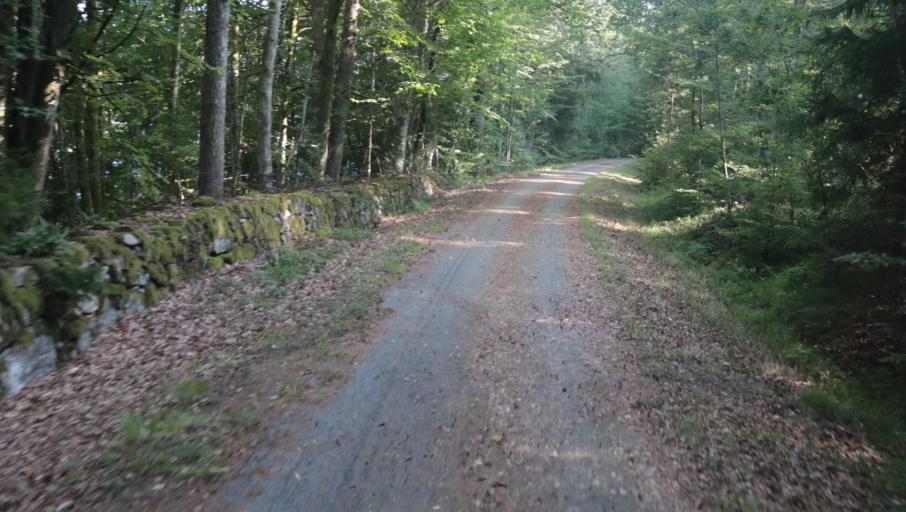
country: SE
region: Blekinge
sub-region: Karlshamns Kommun
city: Svangsta
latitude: 56.3803
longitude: 14.6787
